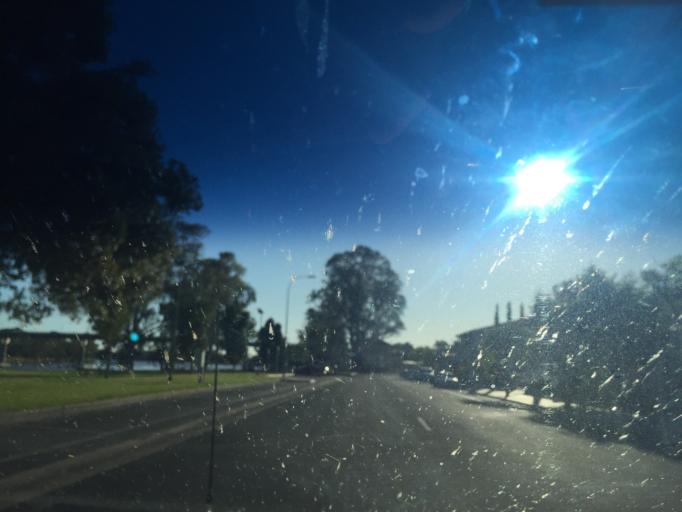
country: AU
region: South Australia
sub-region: Berri and Barmera
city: Berri
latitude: -34.2877
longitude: 140.6024
